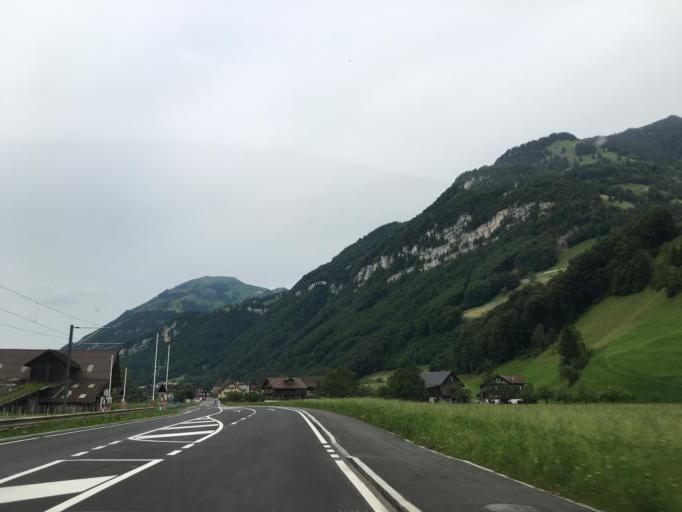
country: CH
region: Nidwalden
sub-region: Nidwalden
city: Wolfenschiessen
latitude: 46.8940
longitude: 8.3883
